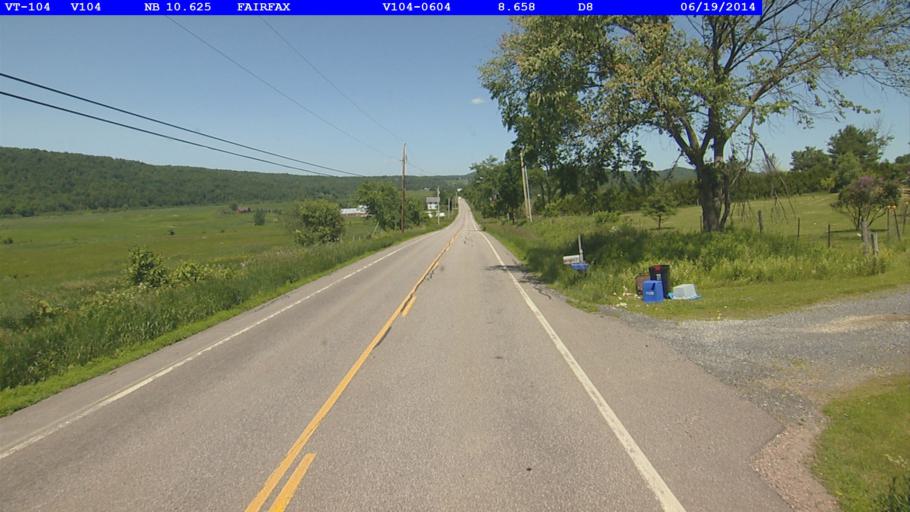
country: US
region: Vermont
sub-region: Chittenden County
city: Milton
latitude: 44.7093
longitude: -73.0375
